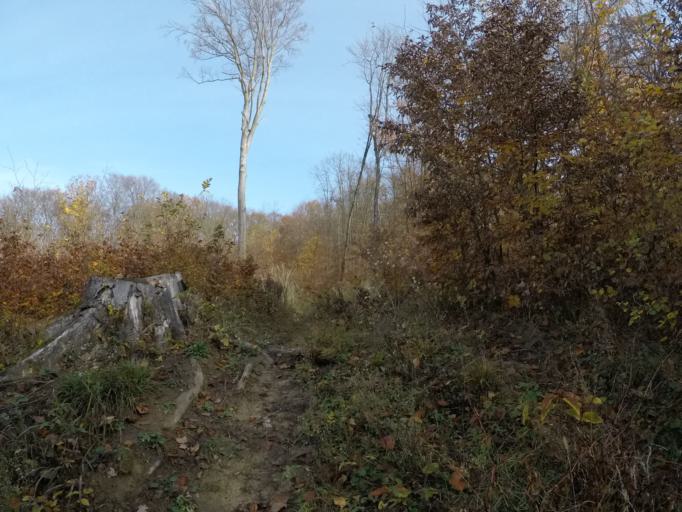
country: SK
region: Presovsky
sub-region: Okres Presov
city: Presov
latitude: 48.9029
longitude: 21.2160
